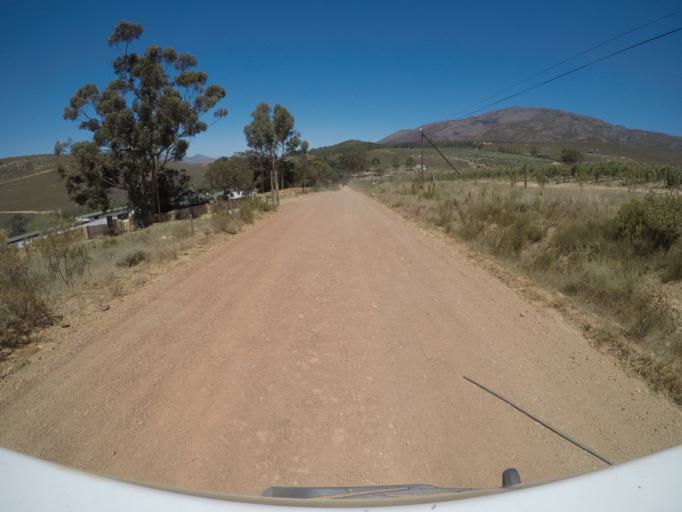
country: ZA
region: Western Cape
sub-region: Overberg District Municipality
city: Caledon
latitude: -34.1782
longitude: 19.2251
